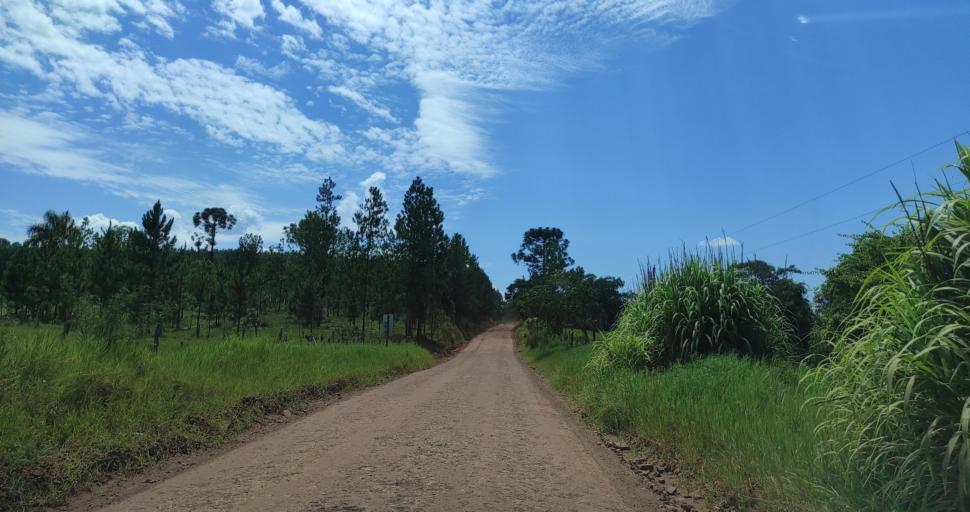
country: AR
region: Misiones
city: Ruiz de Montoya
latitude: -27.0423
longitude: -55.0237
